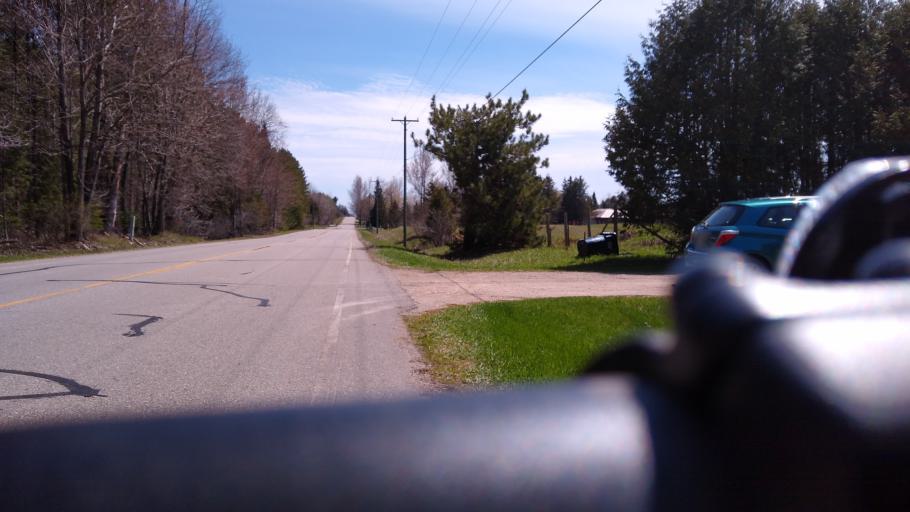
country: US
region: Michigan
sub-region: Delta County
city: Escanaba
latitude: 45.7274
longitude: -87.2025
